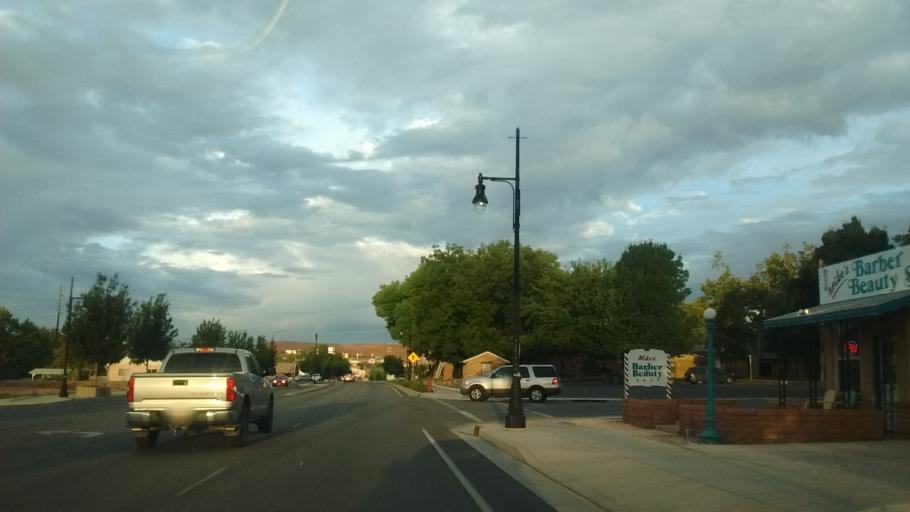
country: US
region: Utah
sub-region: Washington County
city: Washington
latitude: 37.1303
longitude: -113.5079
